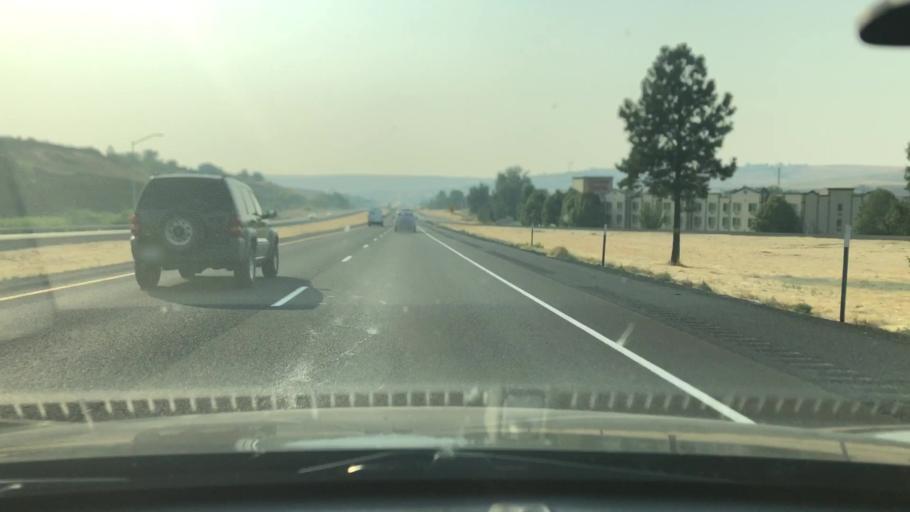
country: US
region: Oregon
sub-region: Umatilla County
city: Pendleton
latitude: 45.6639
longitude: -118.8085
